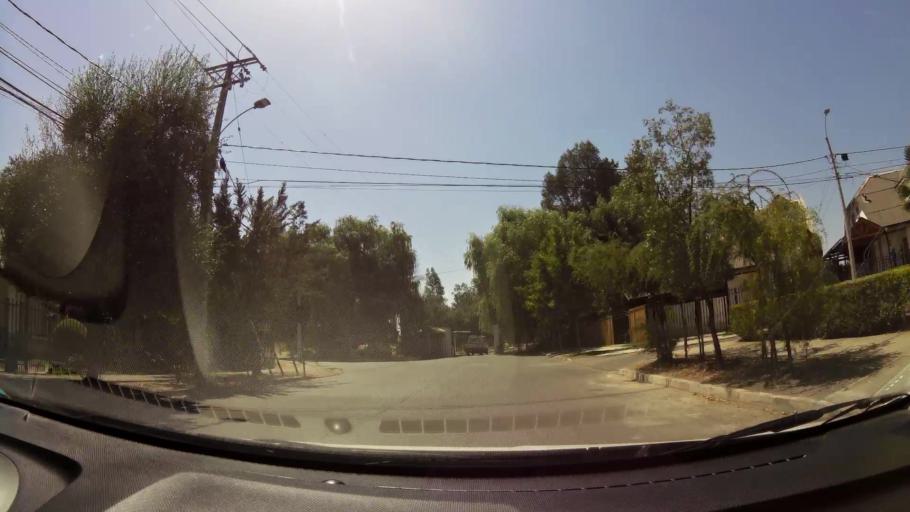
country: CL
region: Maule
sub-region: Provincia de Talca
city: Talca
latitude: -35.4240
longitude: -71.6238
